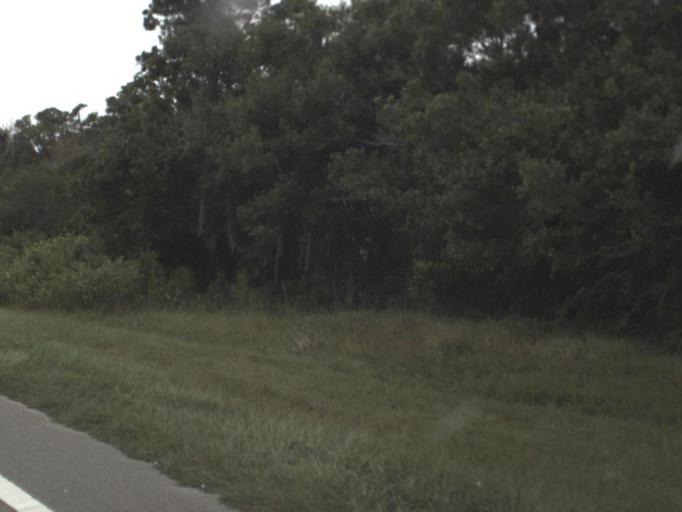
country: US
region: Florida
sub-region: Hillsborough County
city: Wimauma
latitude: 27.5979
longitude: -82.3361
